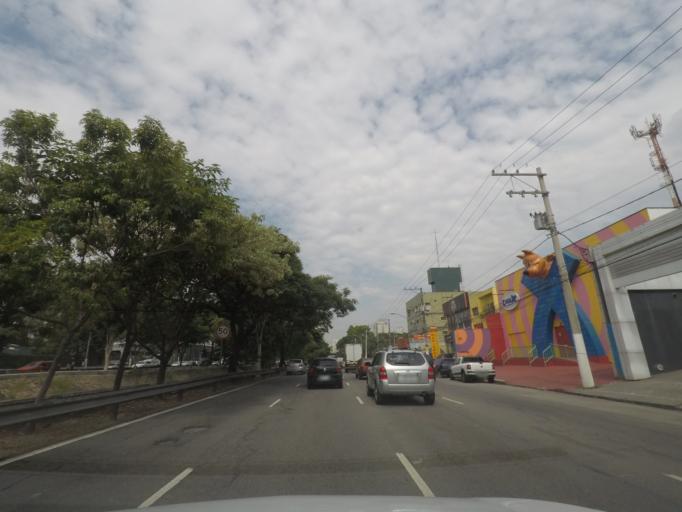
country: BR
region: Sao Paulo
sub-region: Sao Paulo
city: Sao Paulo
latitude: -23.5967
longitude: -46.6224
